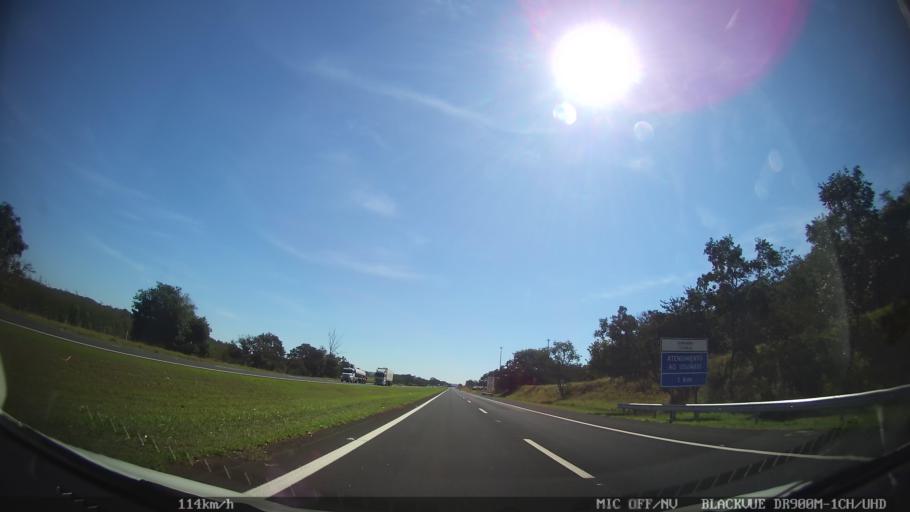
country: BR
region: Sao Paulo
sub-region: Sao Simao
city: Sao Simao
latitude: -21.5585
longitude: -47.6354
